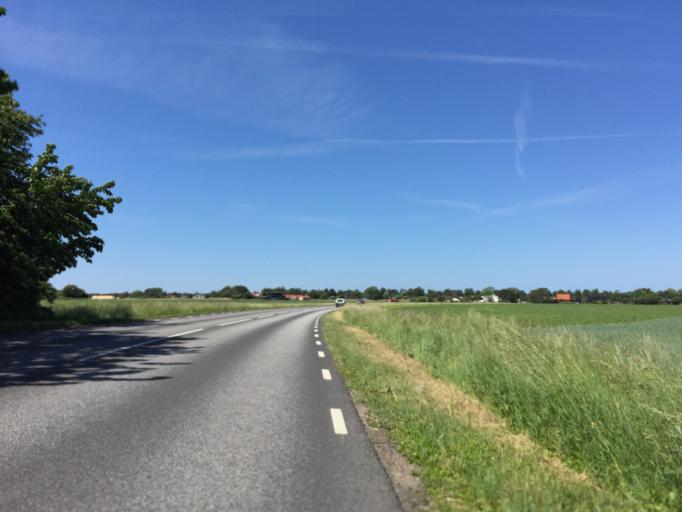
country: SE
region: Skane
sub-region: Vellinge Kommun
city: Hollviken
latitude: 55.3967
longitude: 12.9885
